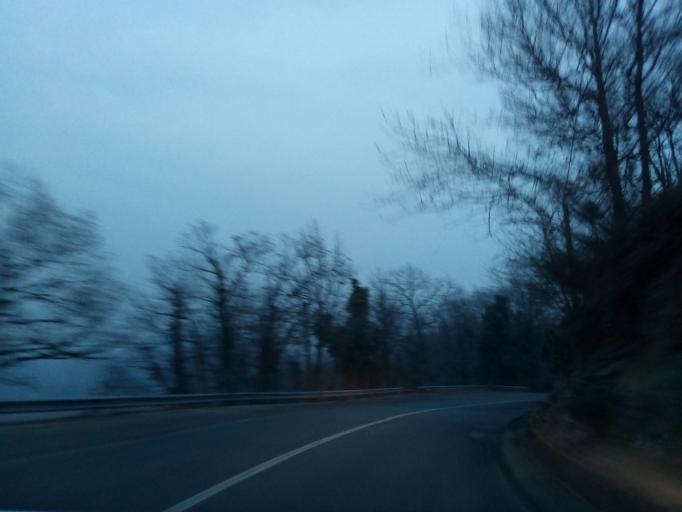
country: IT
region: Piedmont
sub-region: Provincia di Torino
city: Ivrea
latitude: 45.4824
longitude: 7.8821
